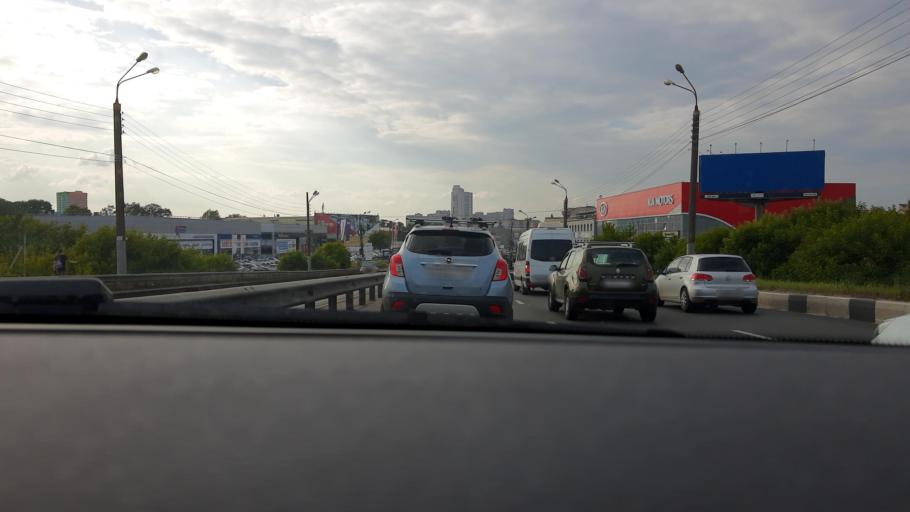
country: RU
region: Nizjnij Novgorod
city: Nizhniy Novgorod
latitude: 56.3057
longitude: 43.8943
